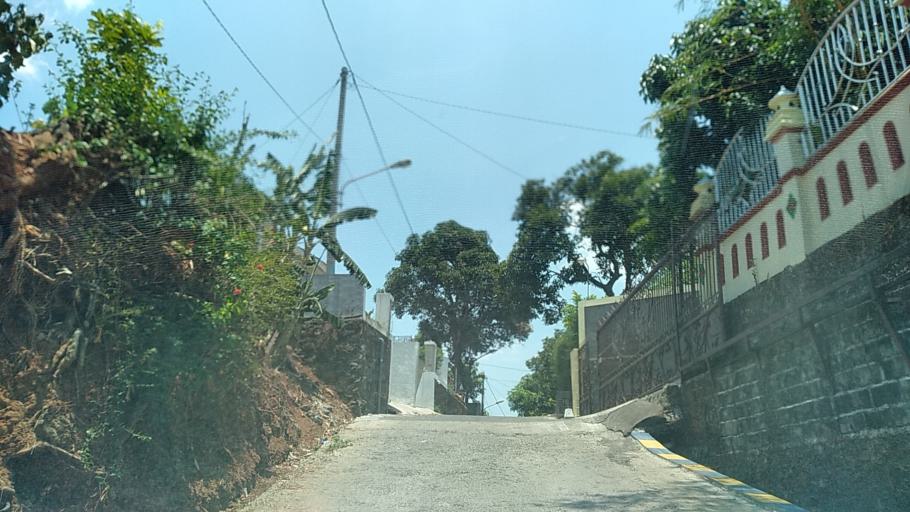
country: ID
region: Central Java
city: Ungaran
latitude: -7.0810
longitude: 110.4281
